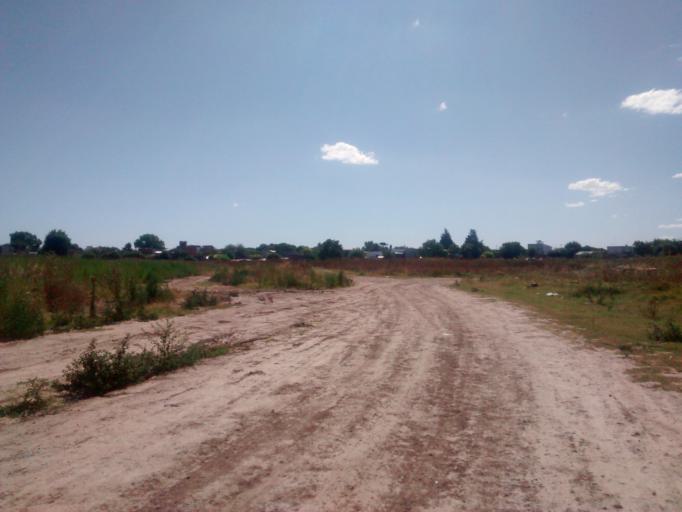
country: AR
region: Buenos Aires
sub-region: Partido de La Plata
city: La Plata
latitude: -34.9340
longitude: -57.9081
